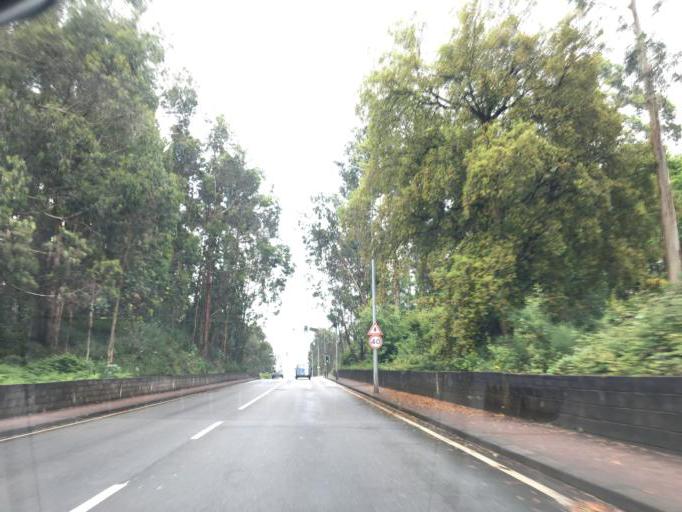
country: PT
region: Porto
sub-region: Maia
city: Nogueira
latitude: 41.2572
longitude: -8.5971
